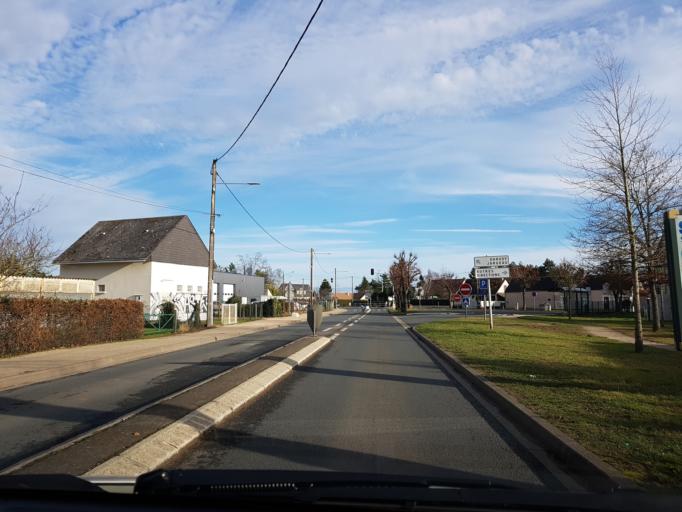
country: FR
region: Centre
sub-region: Departement du Loiret
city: Sandillon
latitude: 47.8472
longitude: 2.0327
